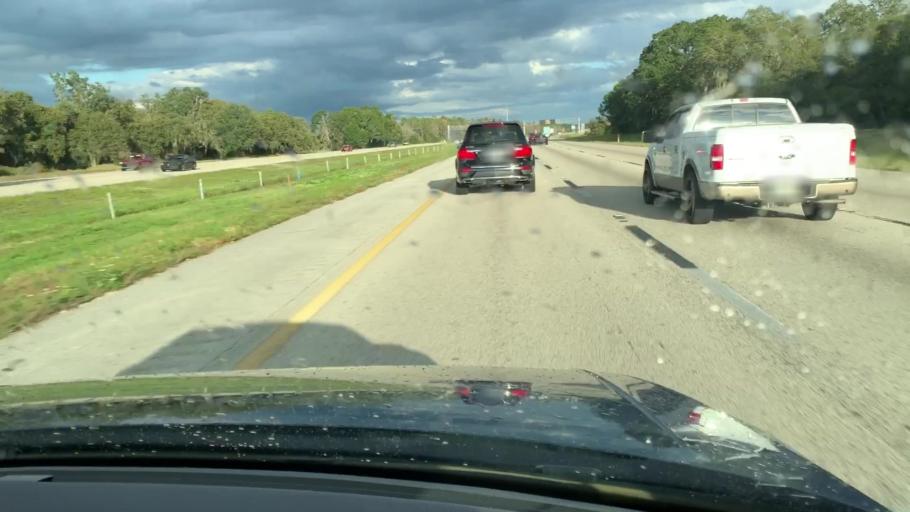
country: US
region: Florida
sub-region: Polk County
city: Polk City
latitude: 28.1556
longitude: -81.8405
